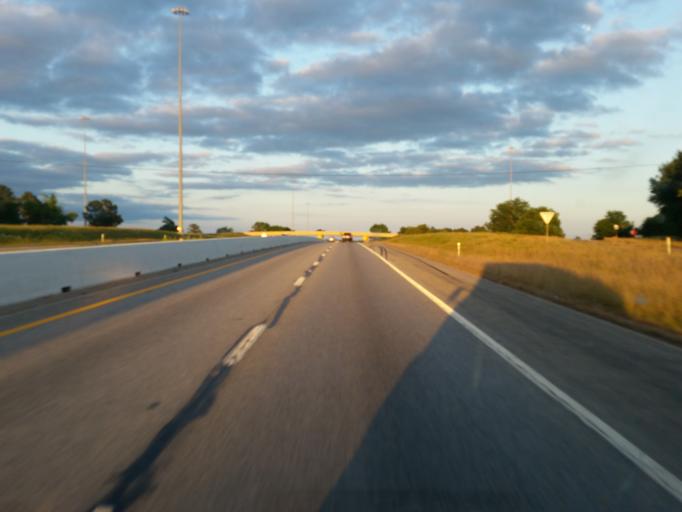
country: US
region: Texas
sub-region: Van Zandt County
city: Van
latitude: 32.5073
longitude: -95.6470
